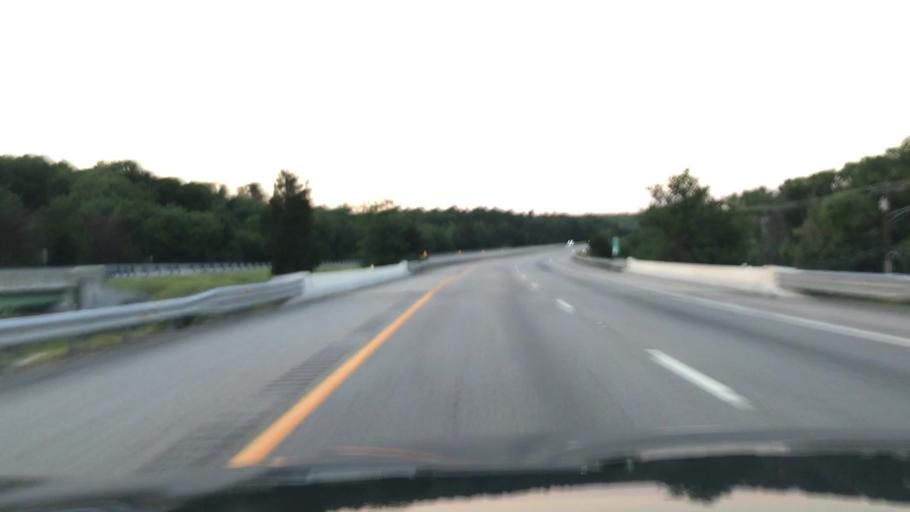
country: US
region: Rhode Island
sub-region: Kent County
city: West Greenwich
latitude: 41.6395
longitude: -71.6252
